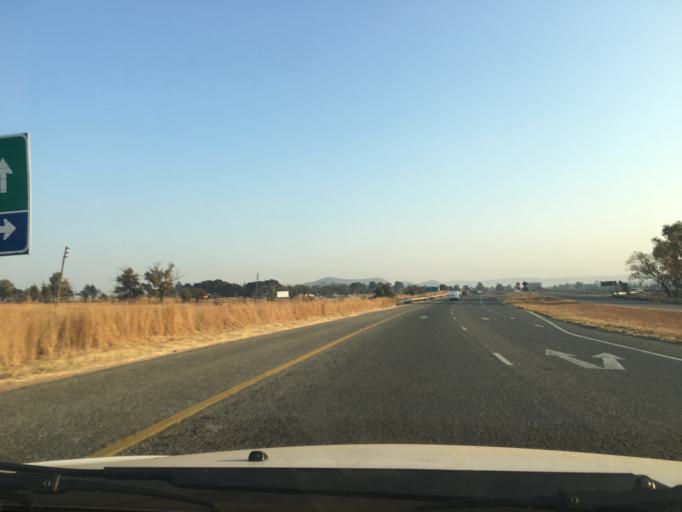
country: ZA
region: Gauteng
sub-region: West Rand District Municipality
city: Muldersdriseloop
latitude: -26.0233
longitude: 27.8616
